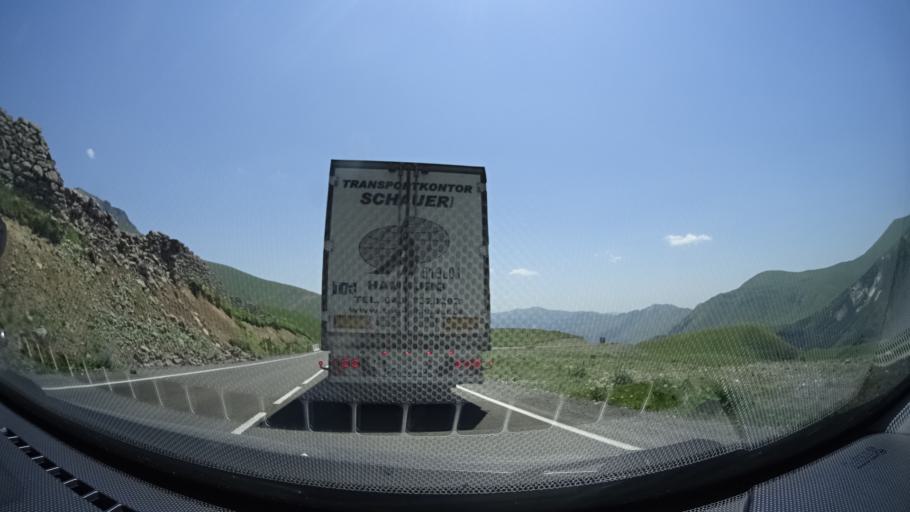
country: GE
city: Gudauri
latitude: 42.4981
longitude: 44.4482
